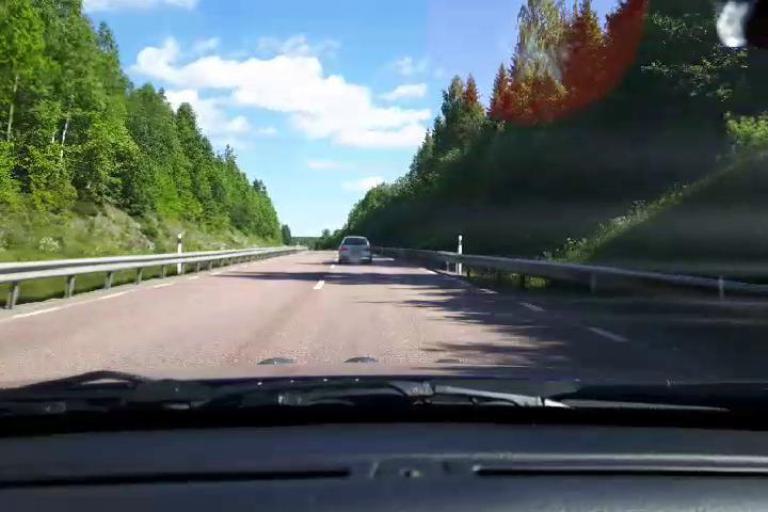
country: SE
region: Gaevleborg
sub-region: Hudiksvalls Kommun
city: Sorforsa
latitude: 61.7406
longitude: 16.8665
